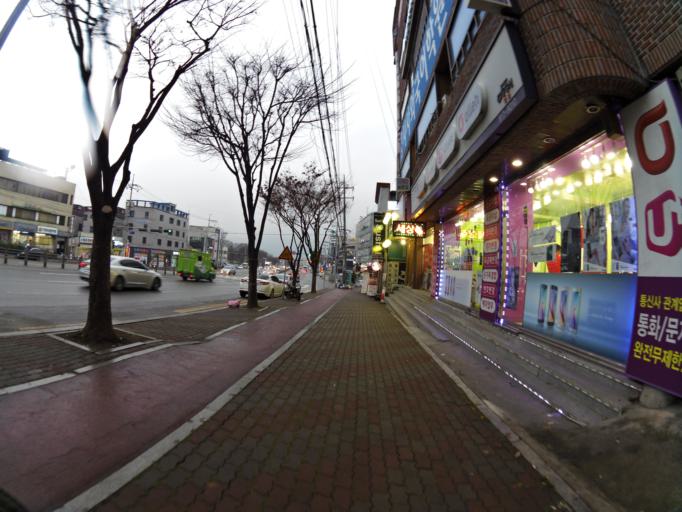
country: KR
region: Gyeongsangbuk-do
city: Gyeongsan-si
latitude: 35.8395
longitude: 128.7569
